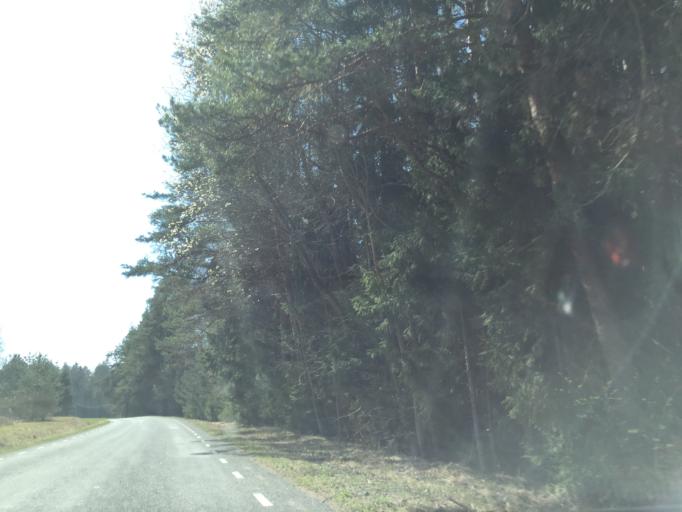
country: EE
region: Viljandimaa
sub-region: Viljandi linn
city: Viljandi
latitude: 58.2902
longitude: 25.5898
